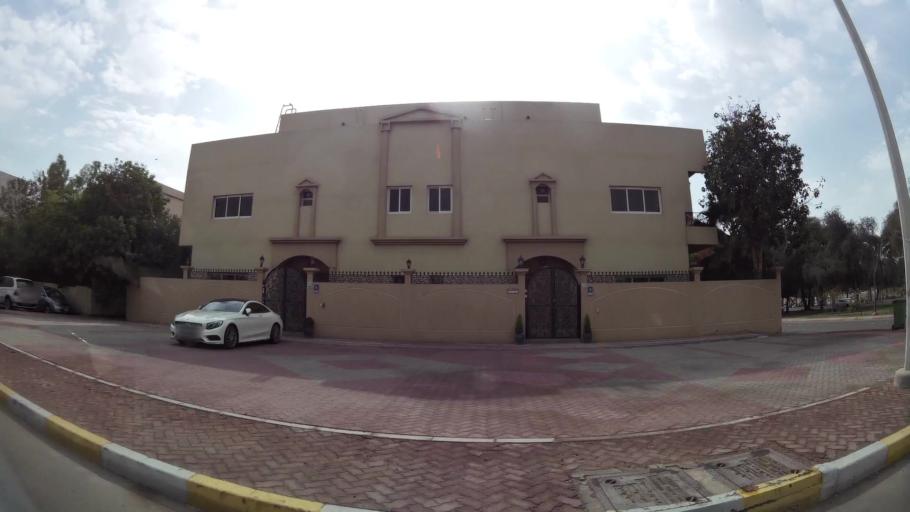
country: AE
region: Abu Dhabi
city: Abu Dhabi
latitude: 24.4572
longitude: 54.3752
